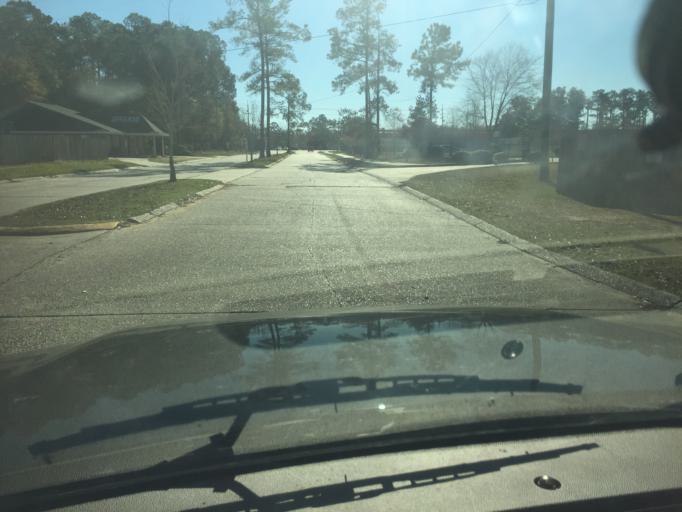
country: US
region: Louisiana
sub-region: Saint Tammany Parish
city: Slidell
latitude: 30.2996
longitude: -89.7619
